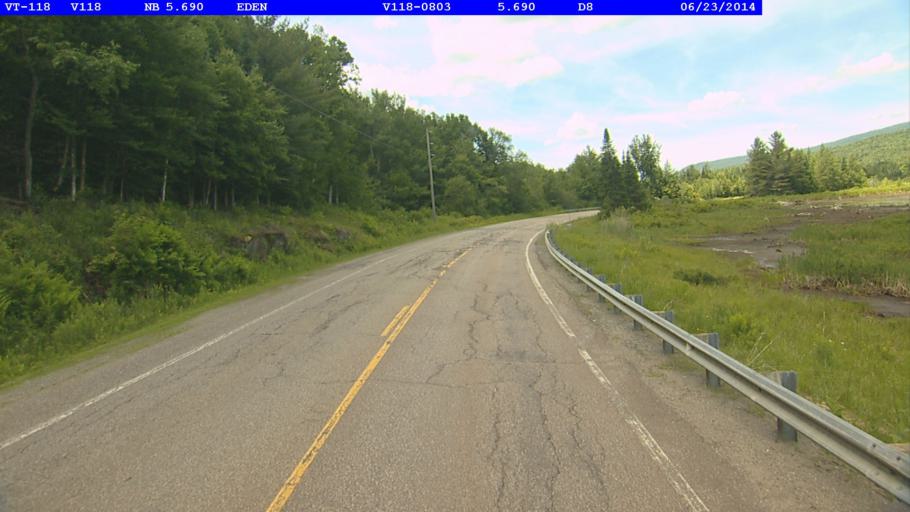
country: US
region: Vermont
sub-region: Lamoille County
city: Johnson
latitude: 44.7641
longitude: -72.6073
